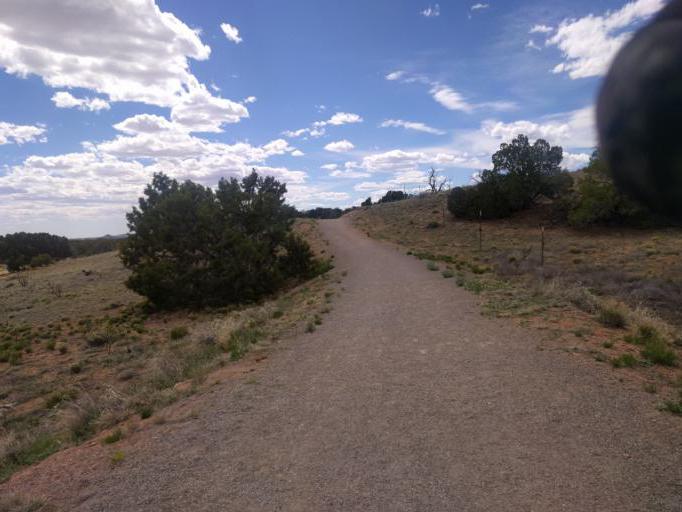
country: US
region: New Mexico
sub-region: Santa Fe County
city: Agua Fria
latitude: 35.5991
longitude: -105.9945
